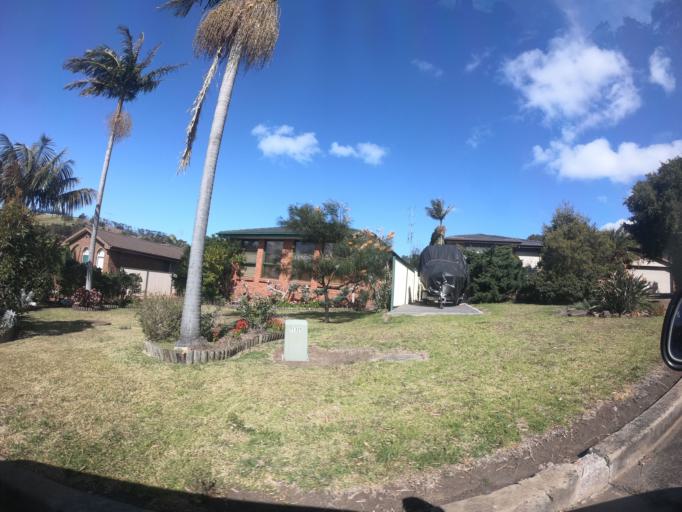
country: AU
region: New South Wales
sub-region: Wollongong
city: Berkeley
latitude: -34.4687
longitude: 150.8418
